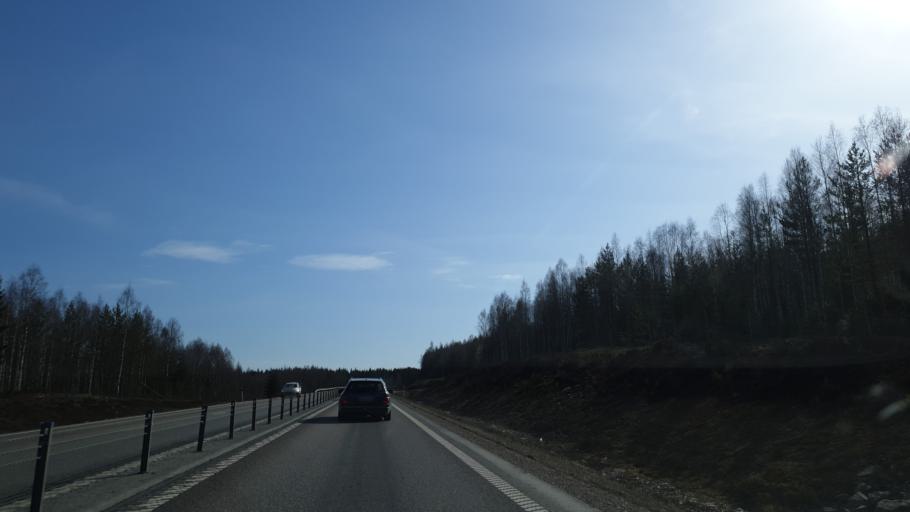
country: SE
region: Vaesternorrland
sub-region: Sundsvalls Kommun
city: Njurundabommen
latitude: 62.1999
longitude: 17.3711
